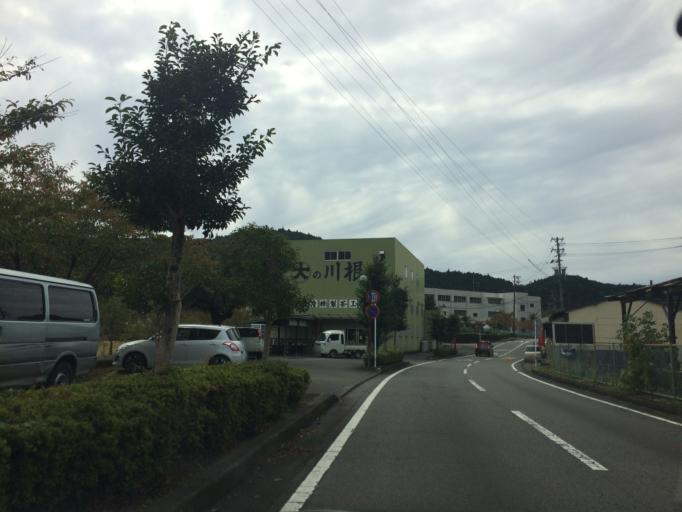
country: JP
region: Shizuoka
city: Fujieda
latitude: 35.1063
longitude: 138.1369
